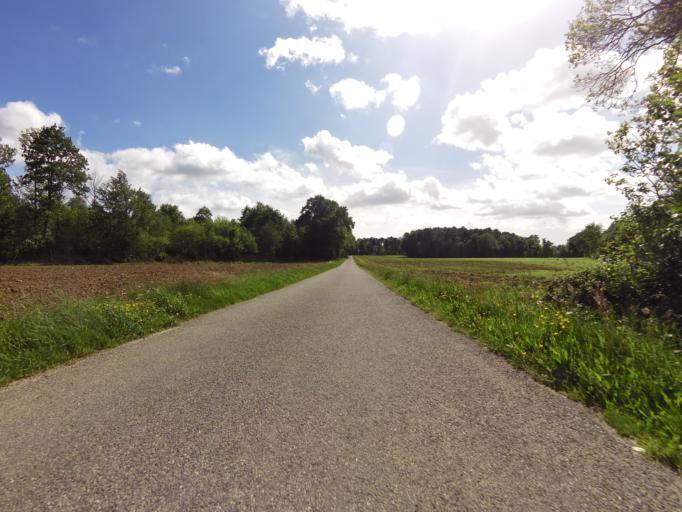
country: FR
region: Brittany
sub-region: Departement du Morbihan
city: Malansac
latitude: 47.7240
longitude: -2.3135
